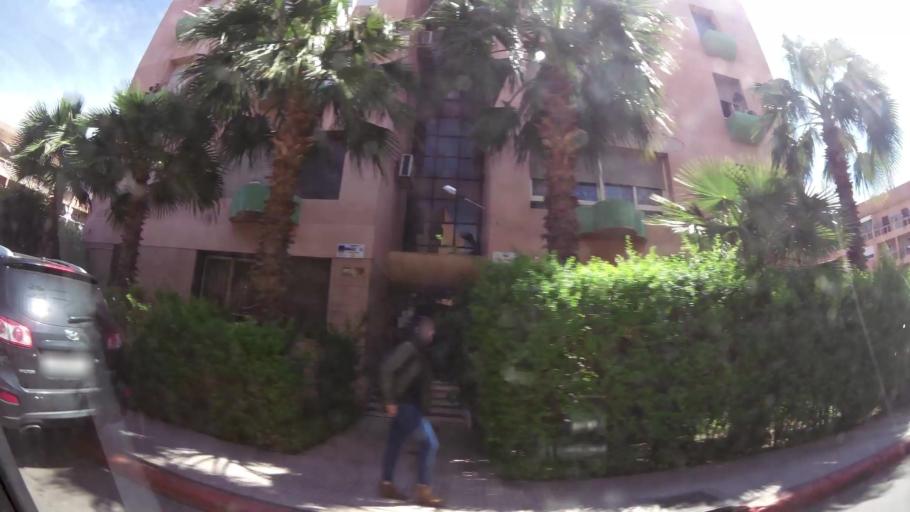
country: MA
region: Marrakech-Tensift-Al Haouz
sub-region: Marrakech
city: Marrakesh
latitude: 31.6622
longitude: -8.0047
